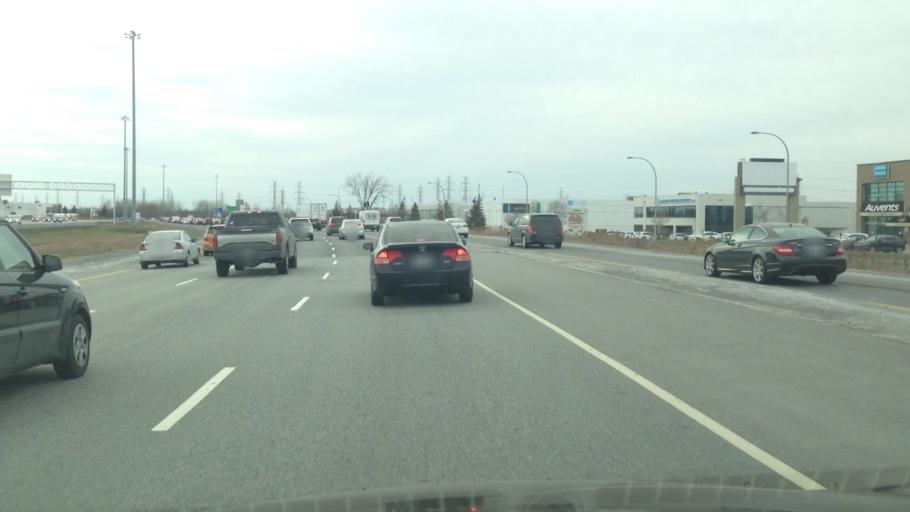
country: CA
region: Quebec
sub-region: Laurentides
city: Rosemere
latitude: 45.5815
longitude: -73.7620
